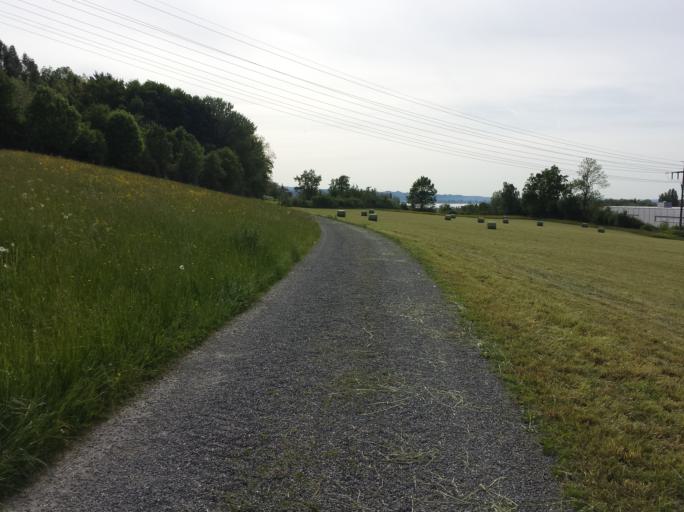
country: CH
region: Saint Gallen
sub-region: Wahlkreis Rheintal
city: Rheineck
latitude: 47.4818
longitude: 9.5537
